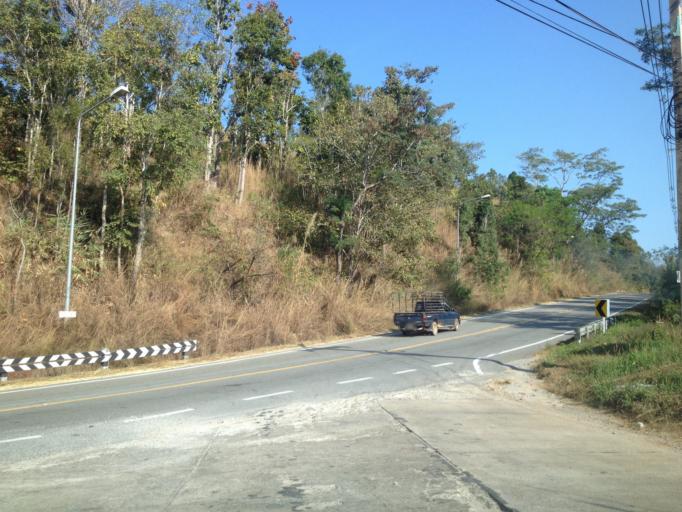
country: TH
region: Mae Hong Son
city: Ban Huai I Huak
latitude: 18.1522
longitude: 98.2140
